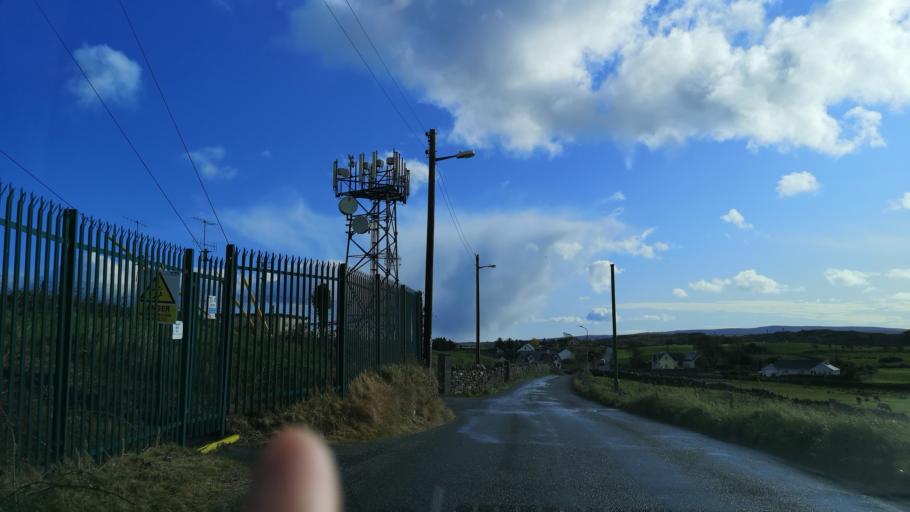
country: IE
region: Connaught
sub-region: Maigh Eo
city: Westport
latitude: 53.7957
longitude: -9.5197
